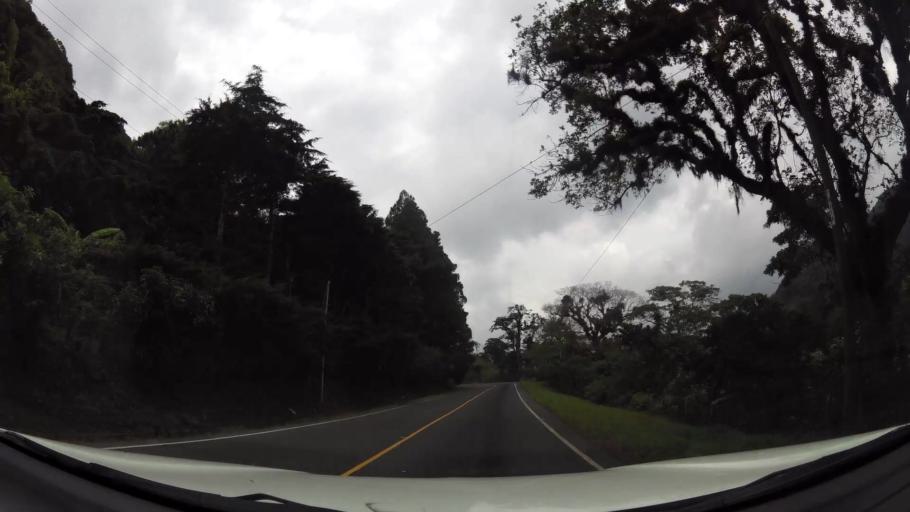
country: NI
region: Matagalpa
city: Matagalpa
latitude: 12.9934
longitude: -85.9206
